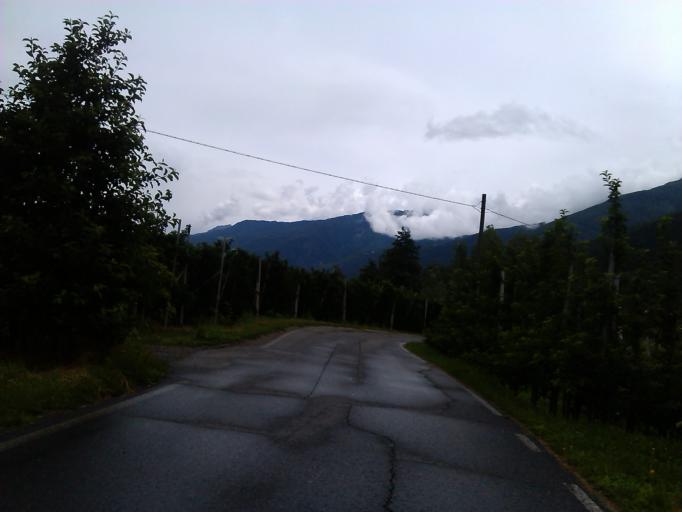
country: IT
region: Trentino-Alto Adige
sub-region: Bolzano
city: Silandro
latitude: 46.6166
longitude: 10.7828
